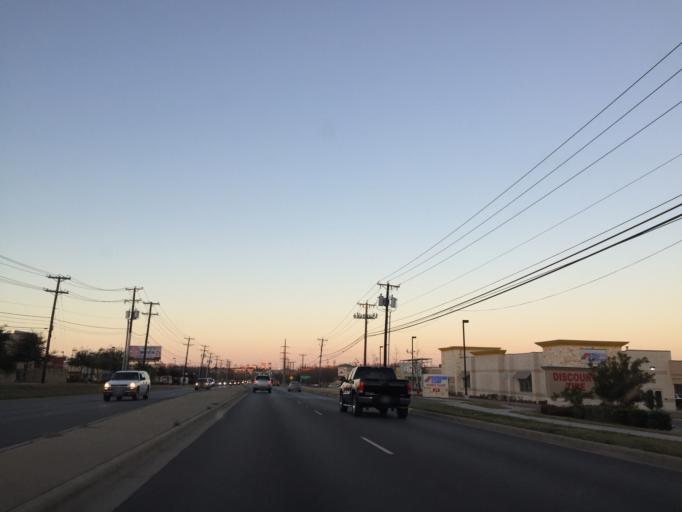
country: US
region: Texas
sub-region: Travis County
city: Pflugerville
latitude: 30.4526
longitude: -97.6039
